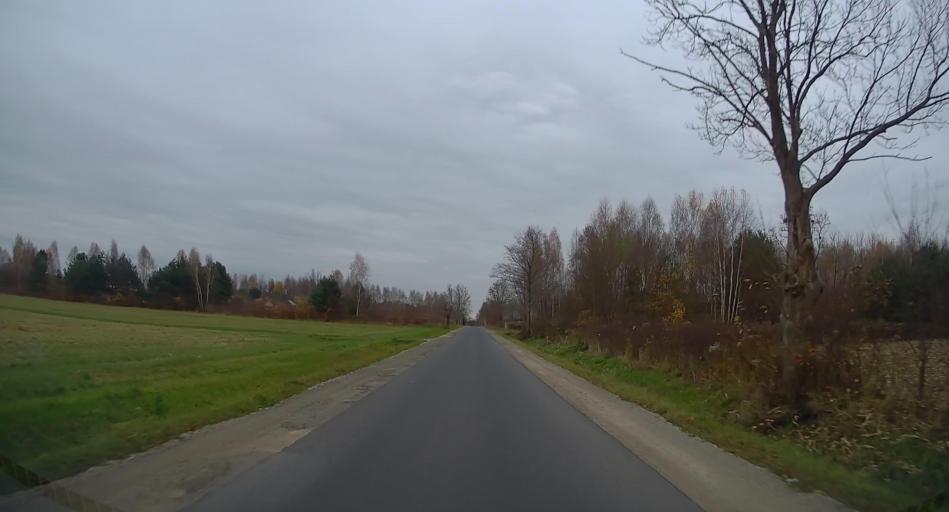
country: PL
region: Lodz Voivodeship
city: Zabia Wola
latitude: 51.9963
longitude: 20.6591
